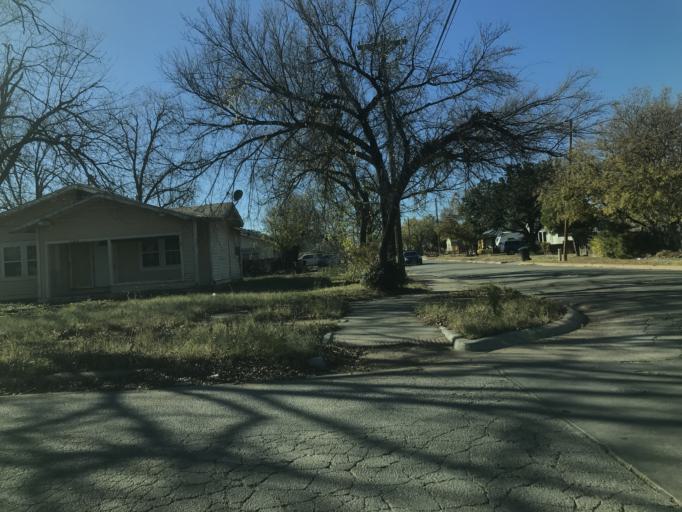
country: US
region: Texas
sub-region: Taylor County
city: Abilene
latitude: 32.4375
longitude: -99.7571
